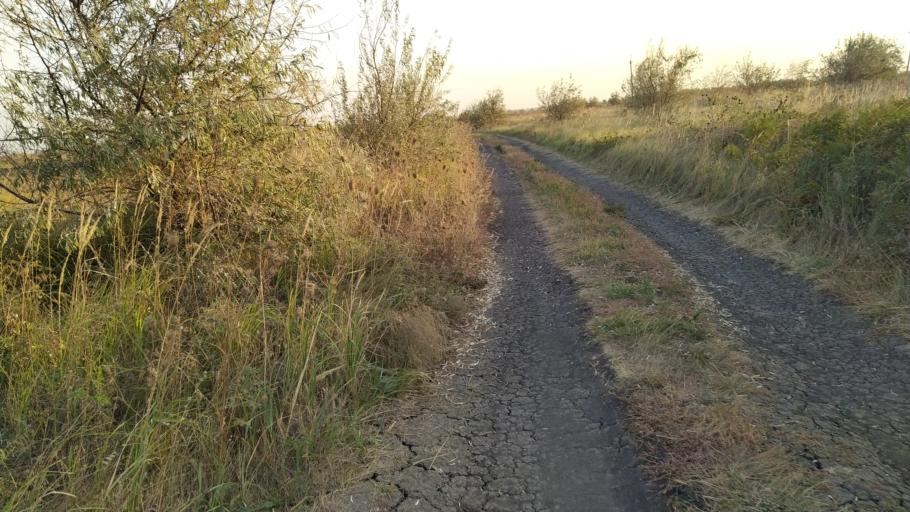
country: RU
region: Rostov
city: Kuleshovka
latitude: 47.1394
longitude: 39.6450
